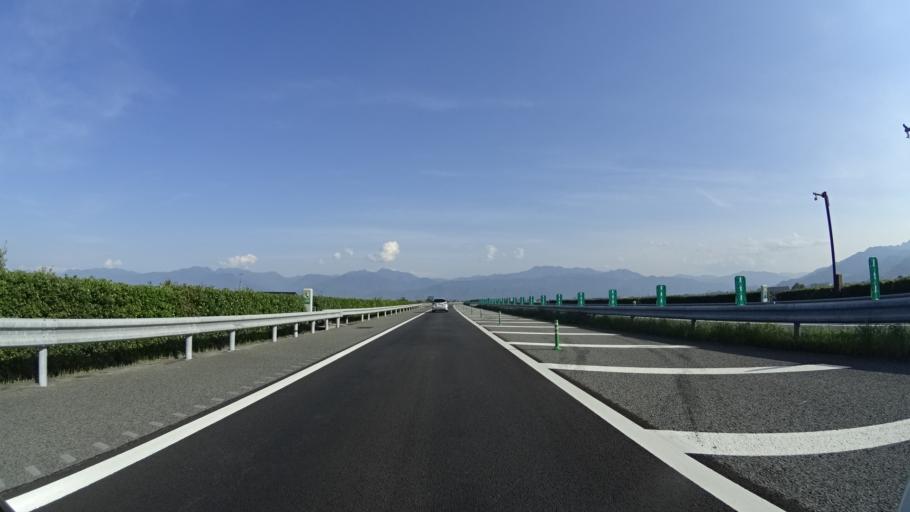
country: JP
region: Ehime
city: Saijo
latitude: 33.9645
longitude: 133.0636
